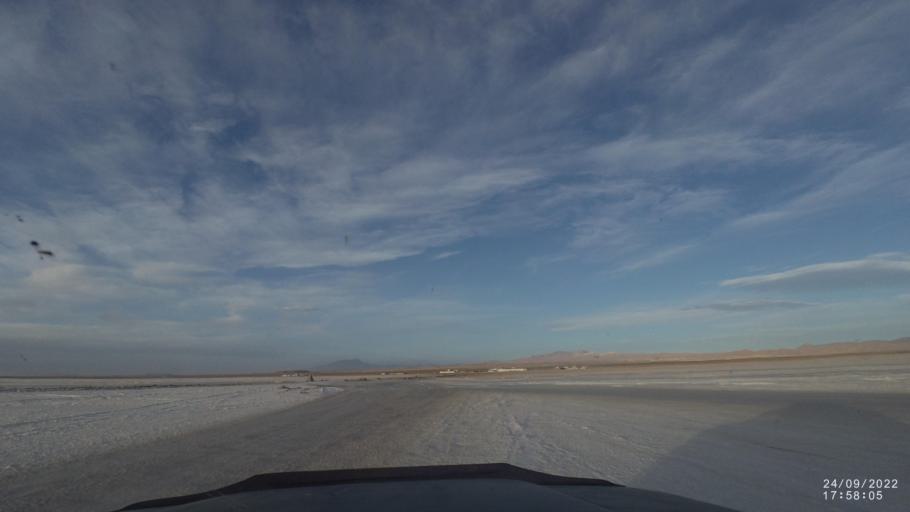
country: BO
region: Potosi
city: Colchani
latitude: -20.3169
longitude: -66.9821
